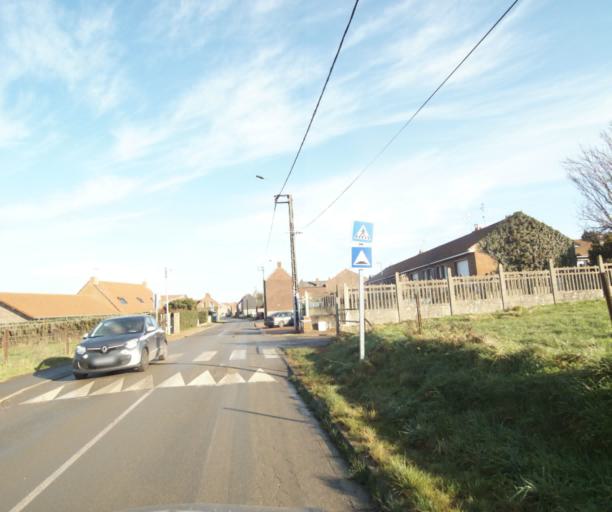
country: FR
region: Nord-Pas-de-Calais
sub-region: Departement du Nord
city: Maing
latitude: 50.3039
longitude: 3.4831
